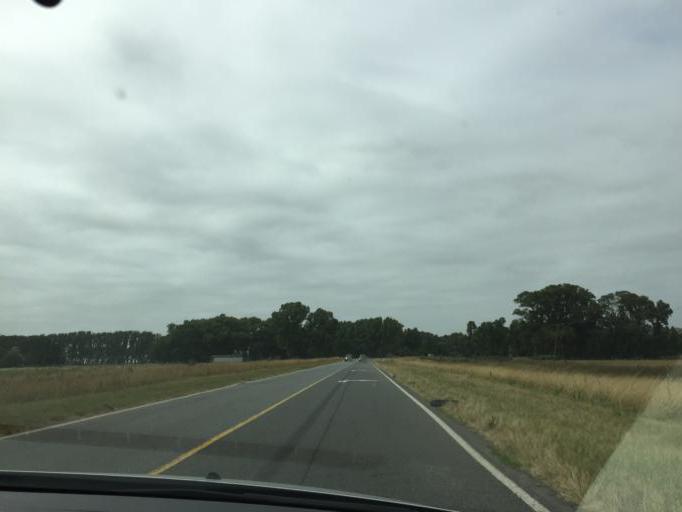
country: AR
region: Buenos Aires
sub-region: Partido de Las Flores
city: Las Flores
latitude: -36.2133
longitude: -59.0457
